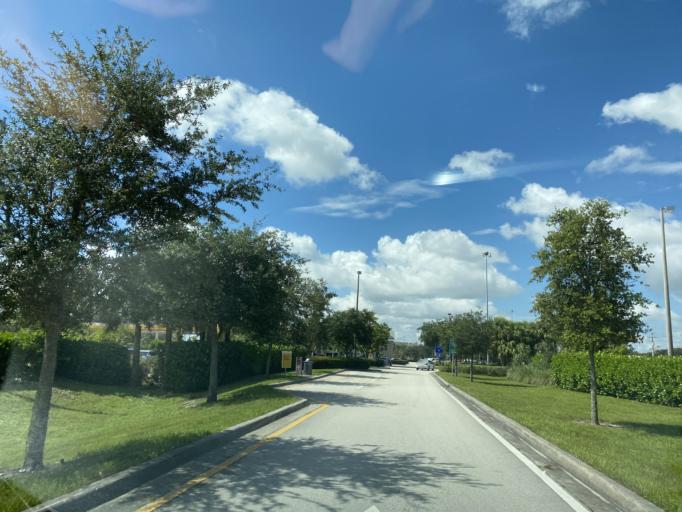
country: US
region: Florida
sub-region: Palm Beach County
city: Greenacres City
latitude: 26.6362
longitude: -80.1752
